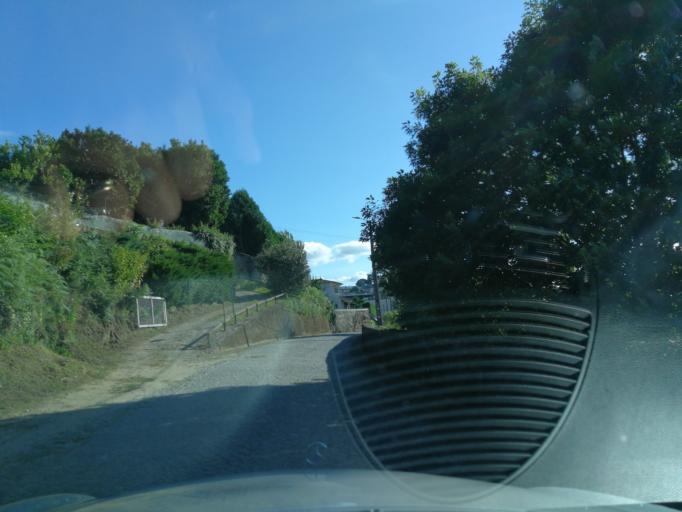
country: PT
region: Braga
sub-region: Braga
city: Adaufe
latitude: 41.5613
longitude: -8.3825
